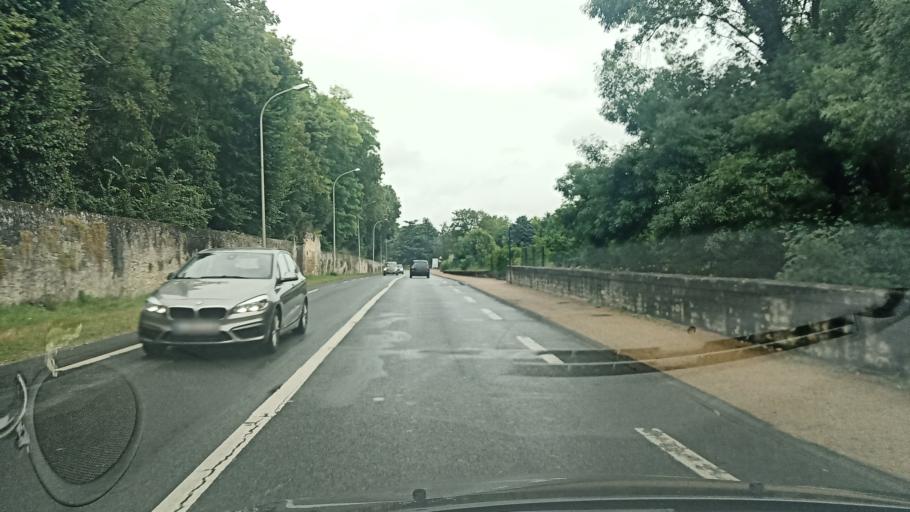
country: FR
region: Poitou-Charentes
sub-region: Departement de la Vienne
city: Poitiers
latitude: 46.6018
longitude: 0.3414
